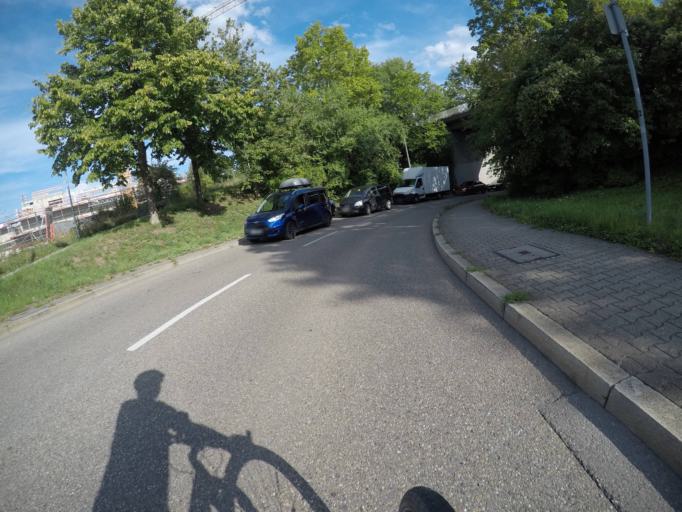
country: DE
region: Baden-Wuerttemberg
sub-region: Regierungsbezirk Stuttgart
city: Stuttgart-Ost
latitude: 48.7987
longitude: 9.2338
